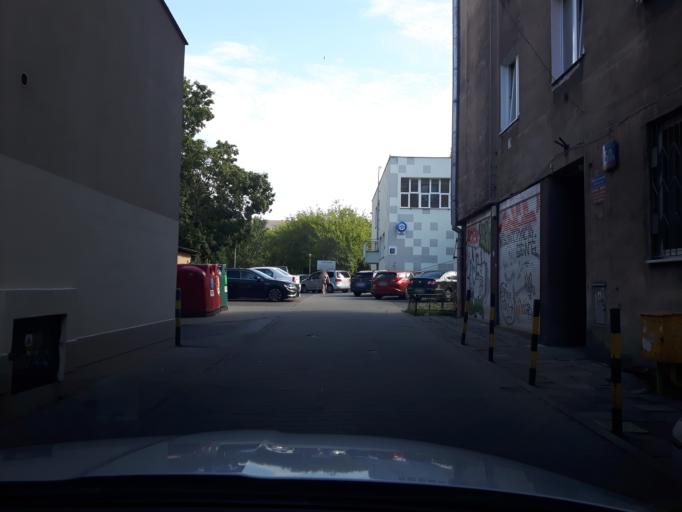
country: PL
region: Masovian Voivodeship
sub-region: Warszawa
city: Praga Polnoc
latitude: 52.2548
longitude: 21.0482
